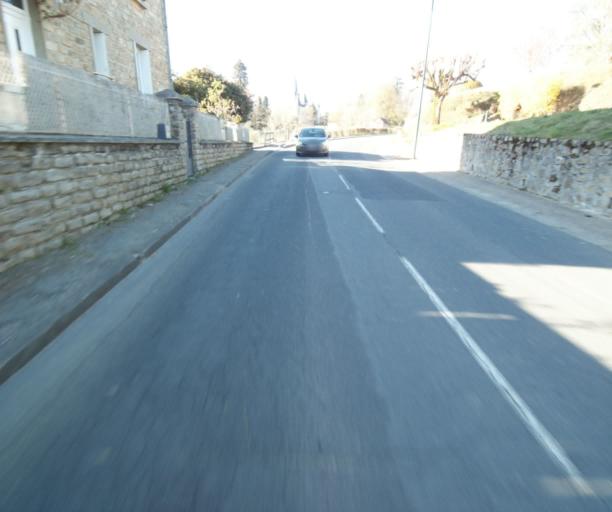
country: FR
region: Limousin
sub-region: Departement de la Correze
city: Seilhac
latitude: 45.3634
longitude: 1.7130
